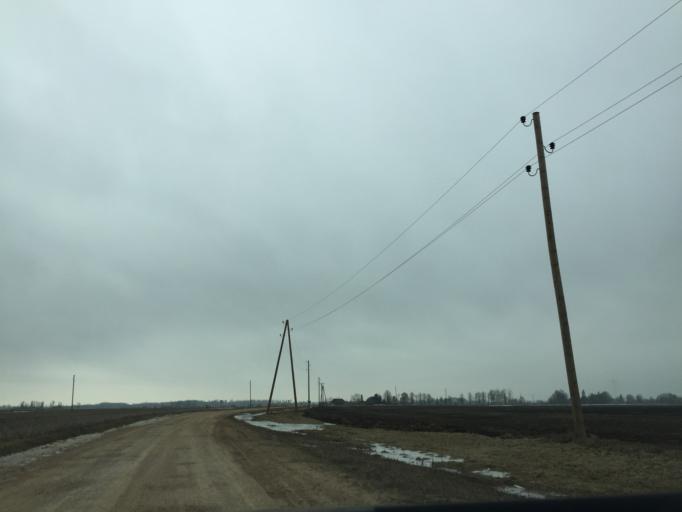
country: LV
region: Rundales
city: Pilsrundale
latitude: 56.5588
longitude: 24.0299
